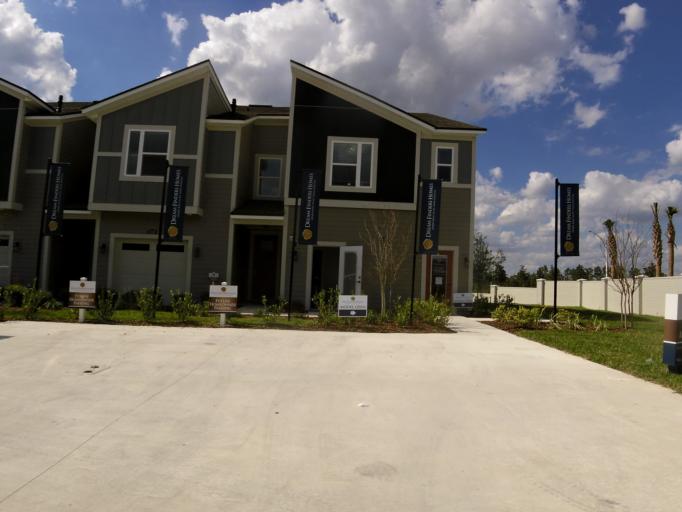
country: US
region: Florida
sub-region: Saint Johns County
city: Palm Valley
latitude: 30.2039
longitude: -81.5104
